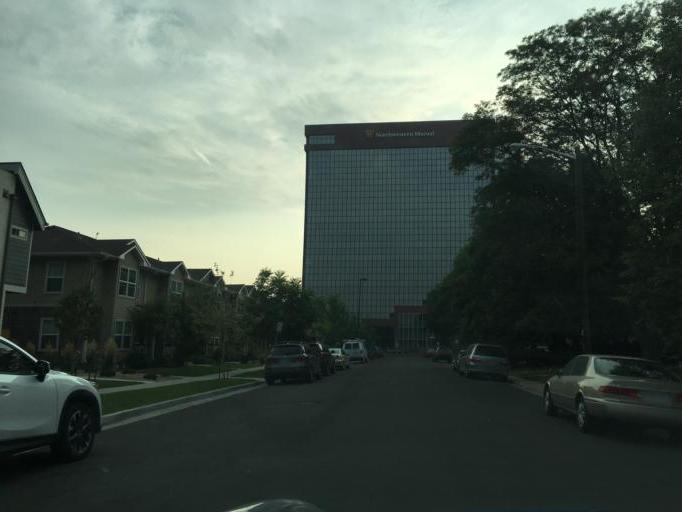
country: US
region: Colorado
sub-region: Arapahoe County
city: Glendale
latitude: 39.6828
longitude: -104.9356
